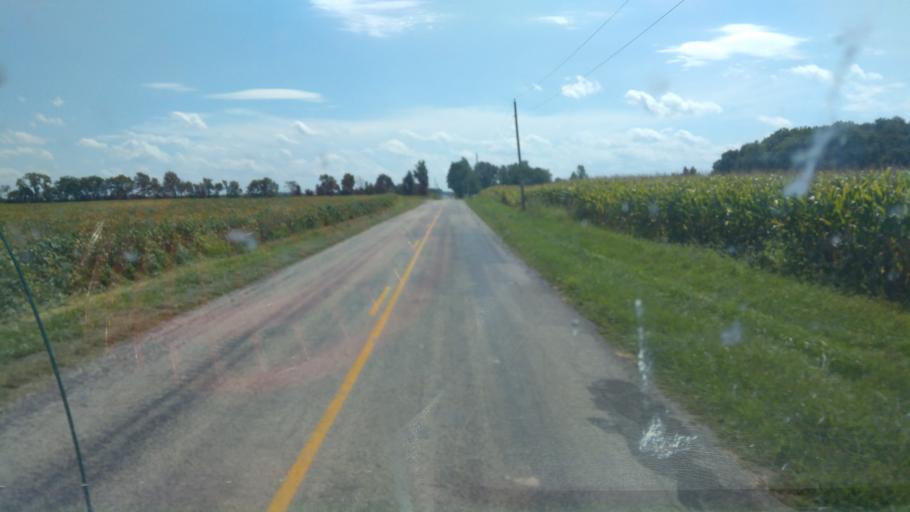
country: US
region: Ohio
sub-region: Wyandot County
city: Upper Sandusky
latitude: 40.6400
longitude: -83.3429
